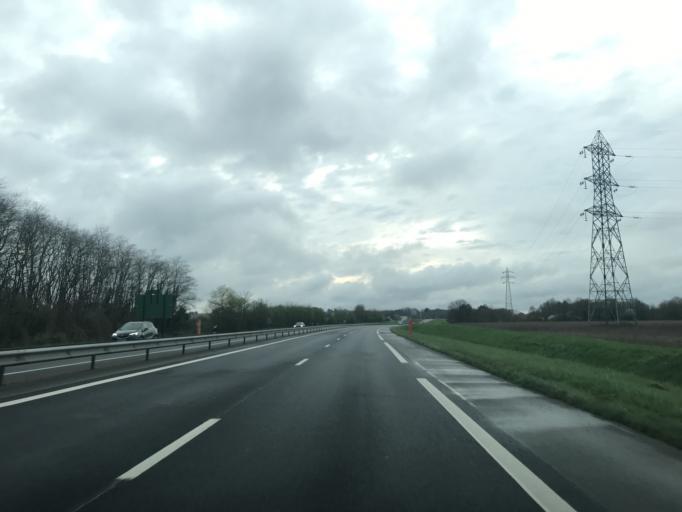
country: FR
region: Centre
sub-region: Departement du Loiret
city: Checy
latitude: 47.9069
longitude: 2.0434
